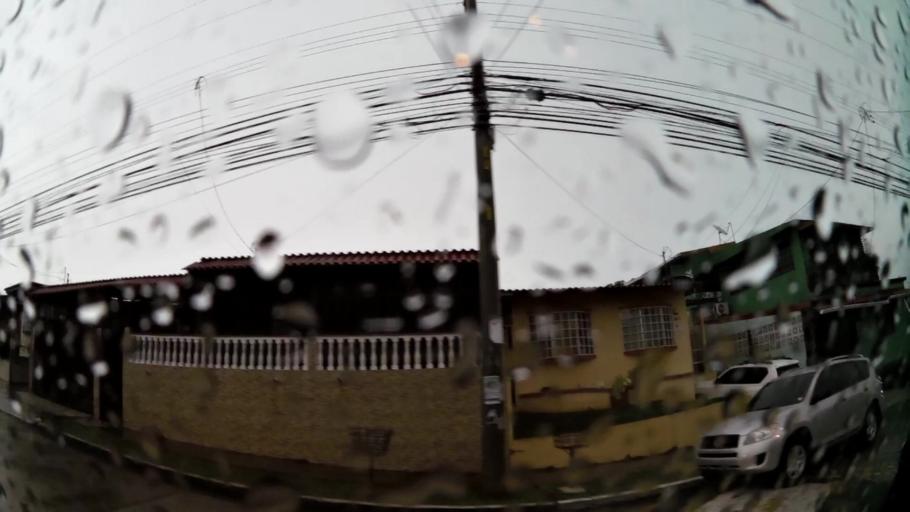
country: PA
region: Panama
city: San Miguelito
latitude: 9.0577
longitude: -79.4736
